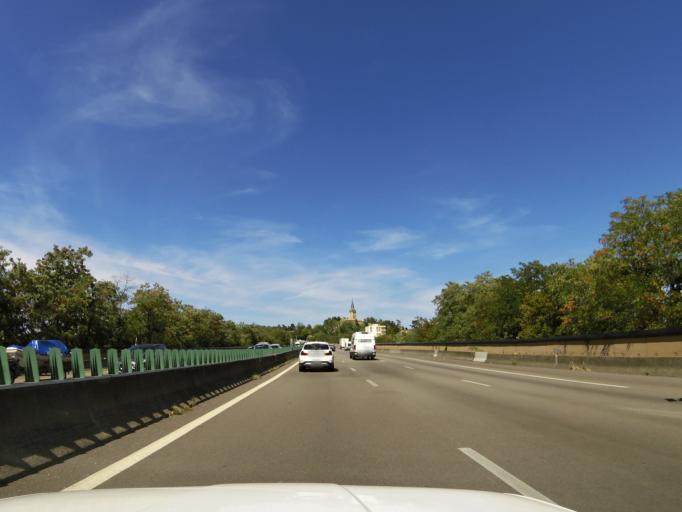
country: FR
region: Rhone-Alpes
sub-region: Departement de l'Isere
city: Roussillon
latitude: 45.3654
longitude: 4.8072
